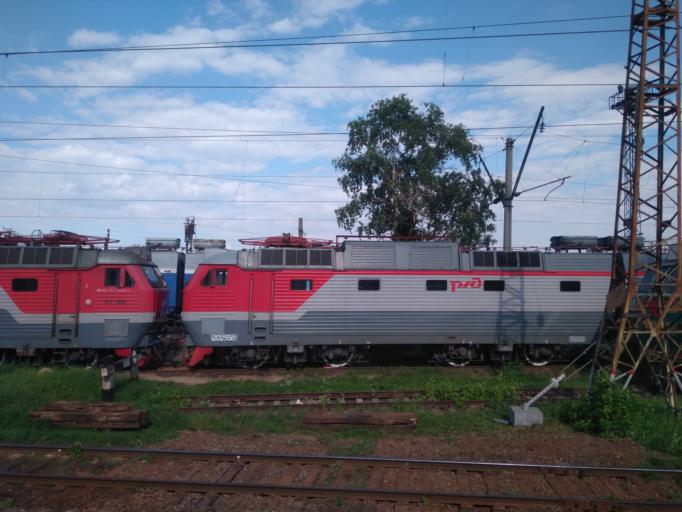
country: RU
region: Moscow
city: Mar'ina Roshcha
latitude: 55.7901
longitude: 37.6422
